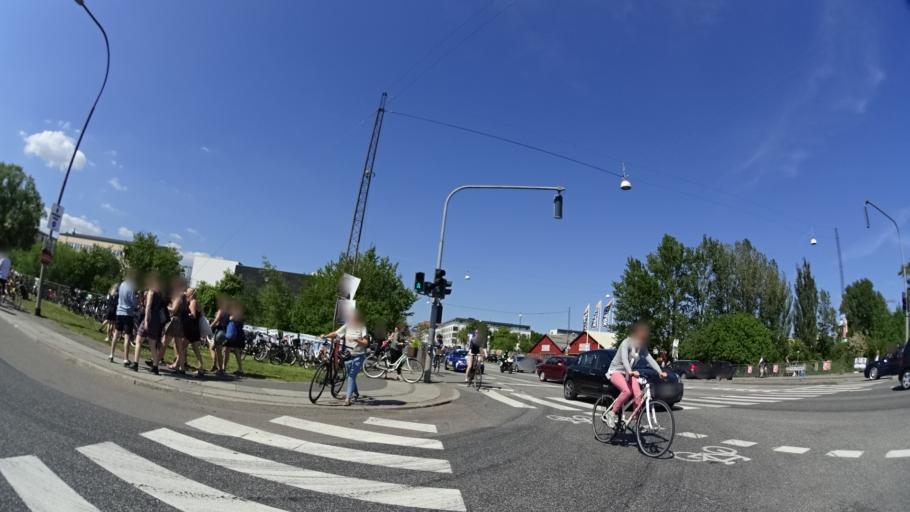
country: DK
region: Central Jutland
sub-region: Arhus Kommune
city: Arhus
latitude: 56.1533
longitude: 10.1824
